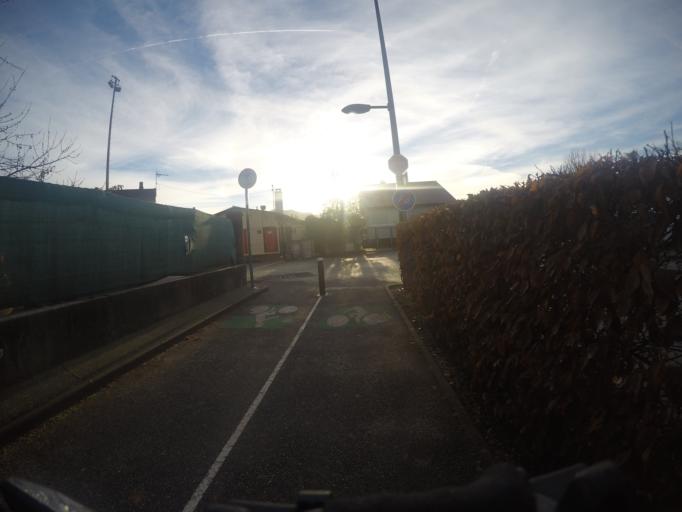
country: FR
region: Rhone-Alpes
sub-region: Departement de la Haute-Savoie
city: Meythet
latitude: 45.9231
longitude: 6.0985
